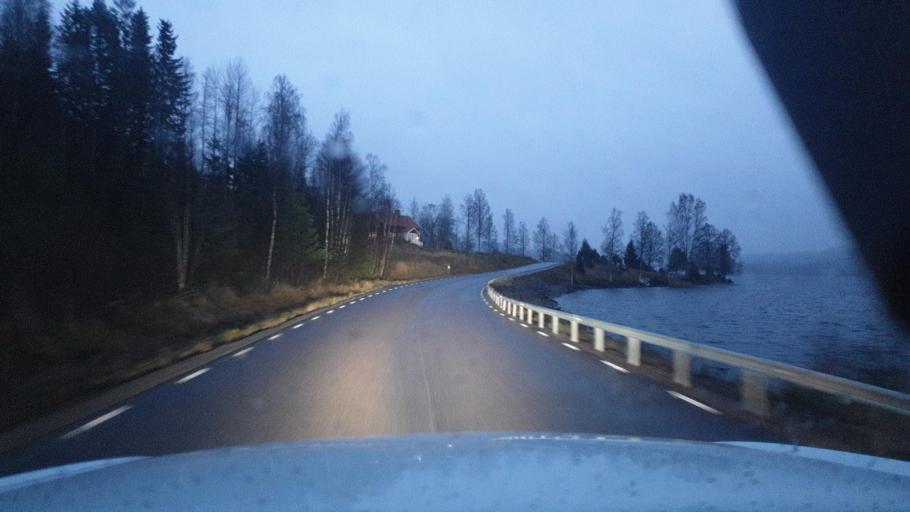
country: SE
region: Vaermland
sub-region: Torsby Kommun
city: Torsby
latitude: 59.9841
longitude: 12.7881
